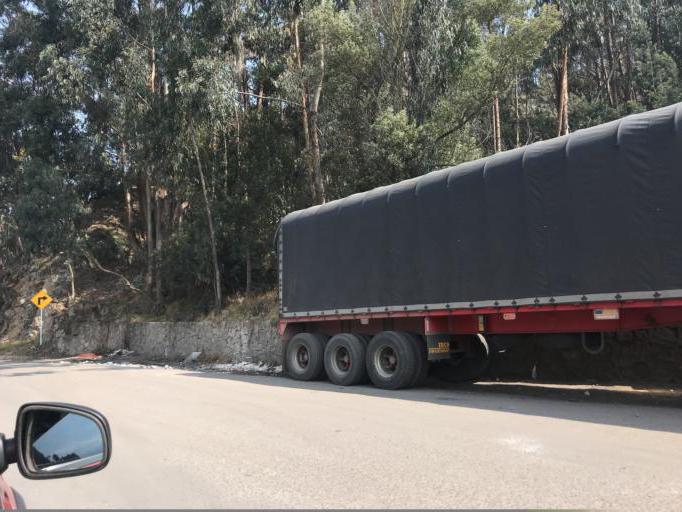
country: CO
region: Boyaca
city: Samaca
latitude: 5.4914
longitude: -73.4798
